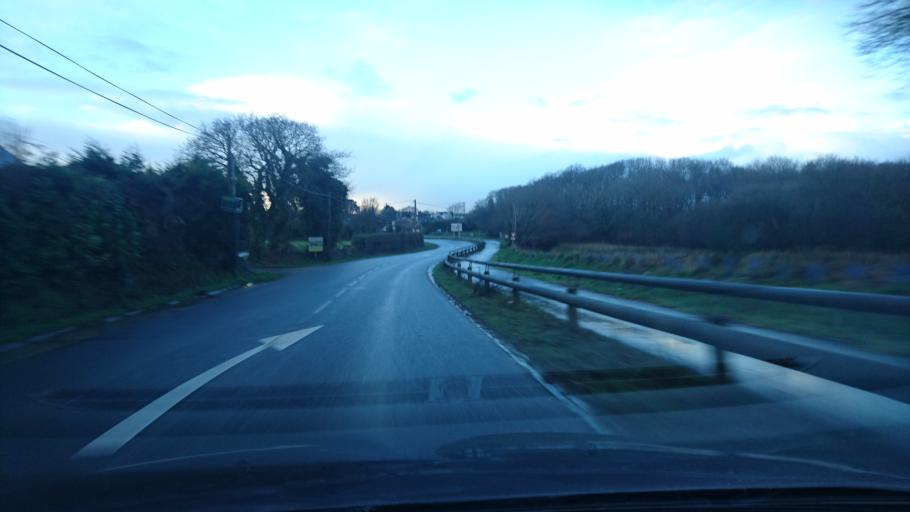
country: FR
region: Brittany
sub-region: Departement du Finistere
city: Guilers
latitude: 48.4156
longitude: -4.5597
